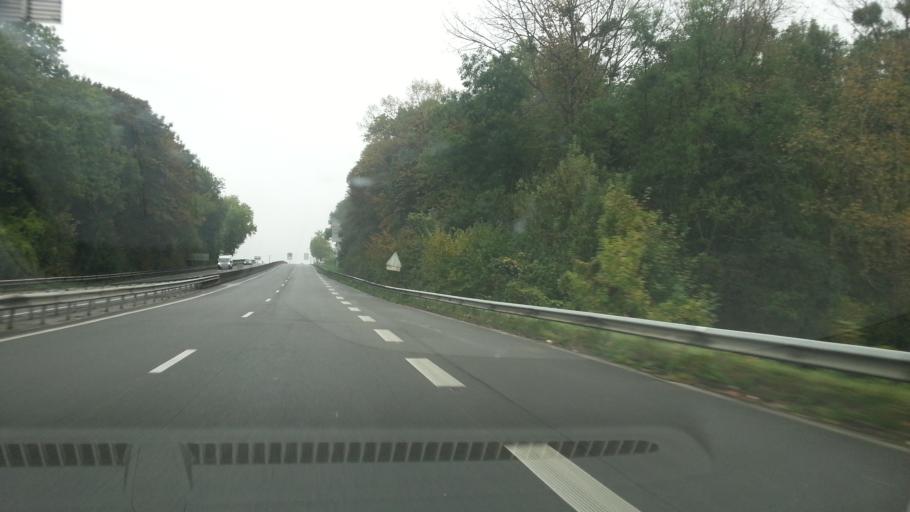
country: FR
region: Picardie
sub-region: Departement de l'Oise
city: Breuil-le-Vert
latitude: 49.3568
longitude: 2.4246
